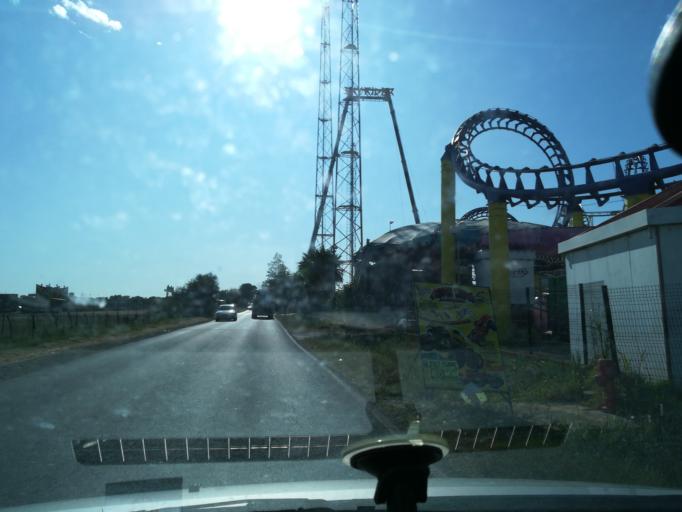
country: FR
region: Languedoc-Roussillon
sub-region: Departement de l'Herault
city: Vias
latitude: 43.3007
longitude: 3.4111
